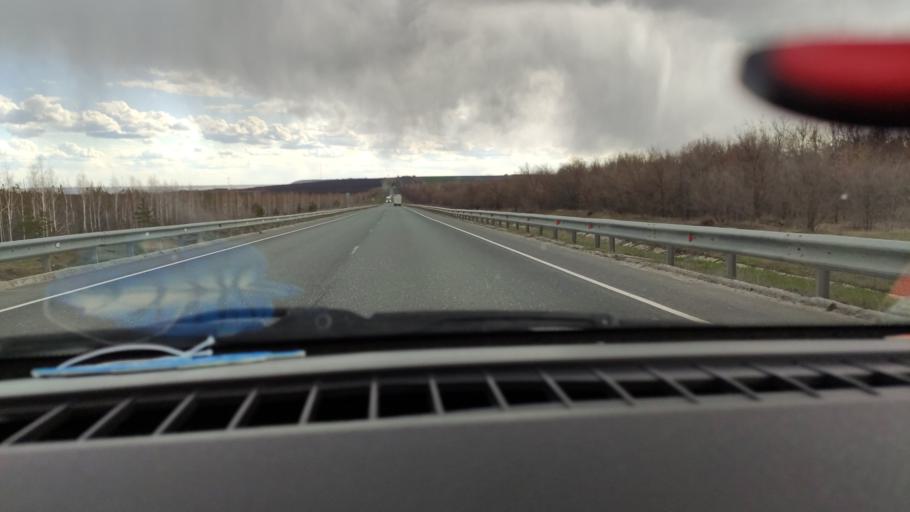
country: RU
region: Saratov
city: Balakovo
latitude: 52.1504
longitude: 47.8107
